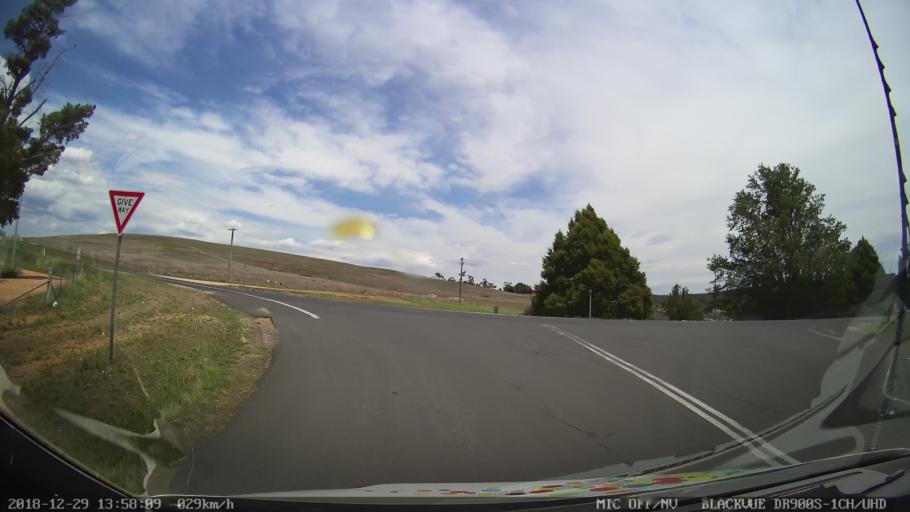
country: AU
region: New South Wales
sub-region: Cooma-Monaro
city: Cooma
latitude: -36.2434
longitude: 149.1371
